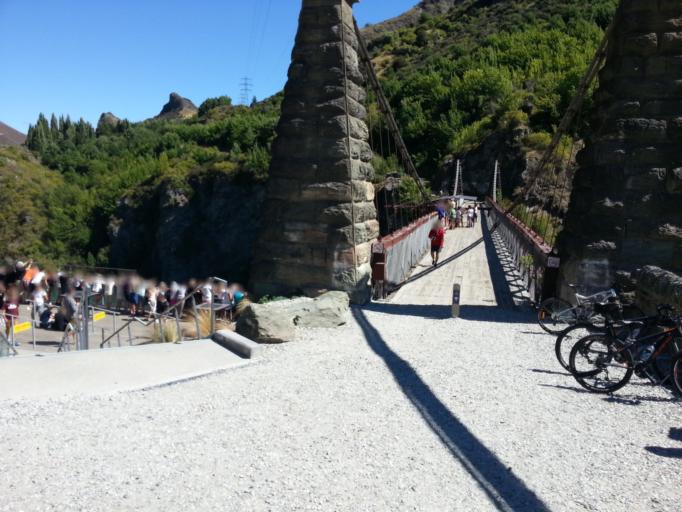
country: NZ
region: Otago
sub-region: Queenstown-Lakes District
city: Arrowtown
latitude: -45.0092
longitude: 168.9004
